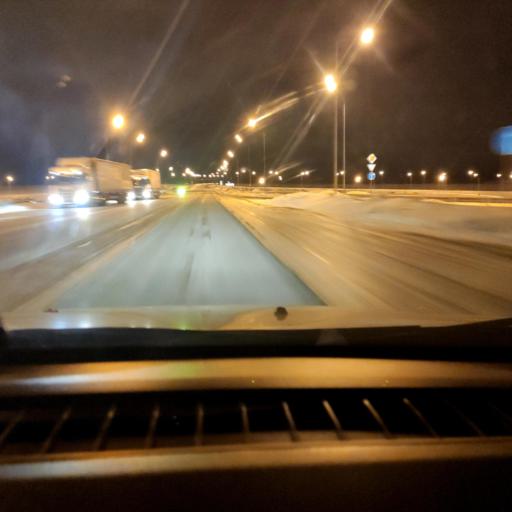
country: RU
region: Samara
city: Smyshlyayevka
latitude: 53.1499
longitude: 50.3942
